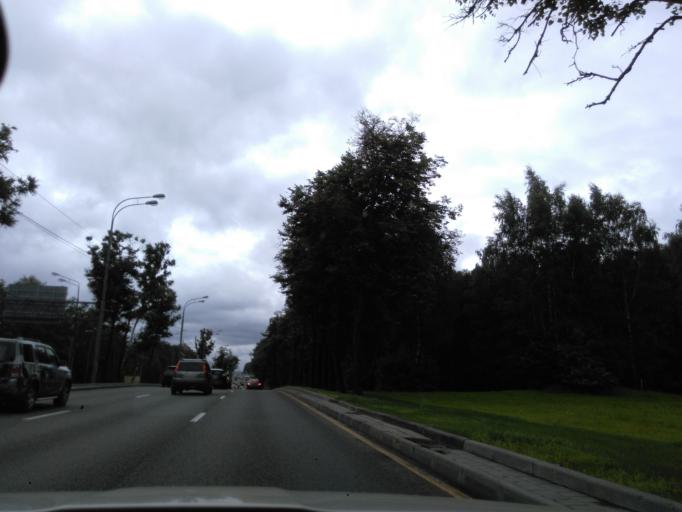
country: RU
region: Moscow
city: Rublevo
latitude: 55.7610
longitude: 37.3882
